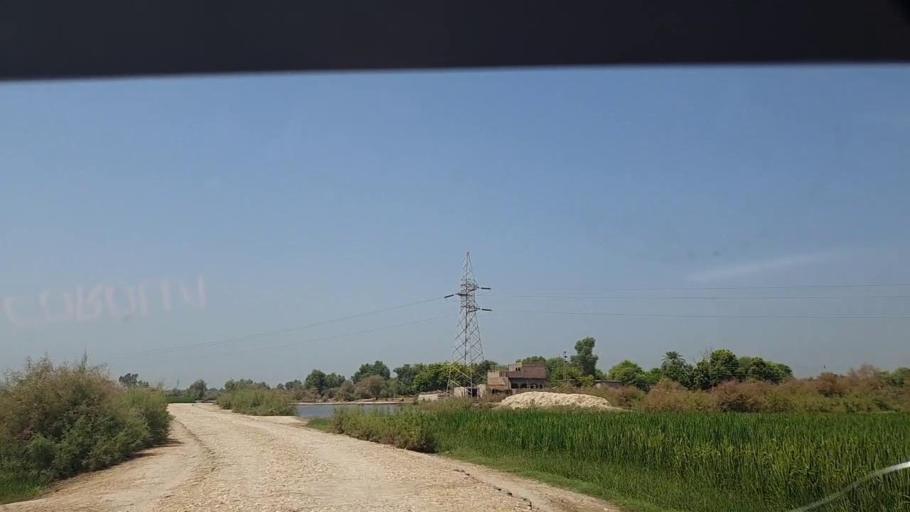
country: PK
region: Sindh
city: Ghauspur
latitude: 28.1868
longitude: 69.0899
